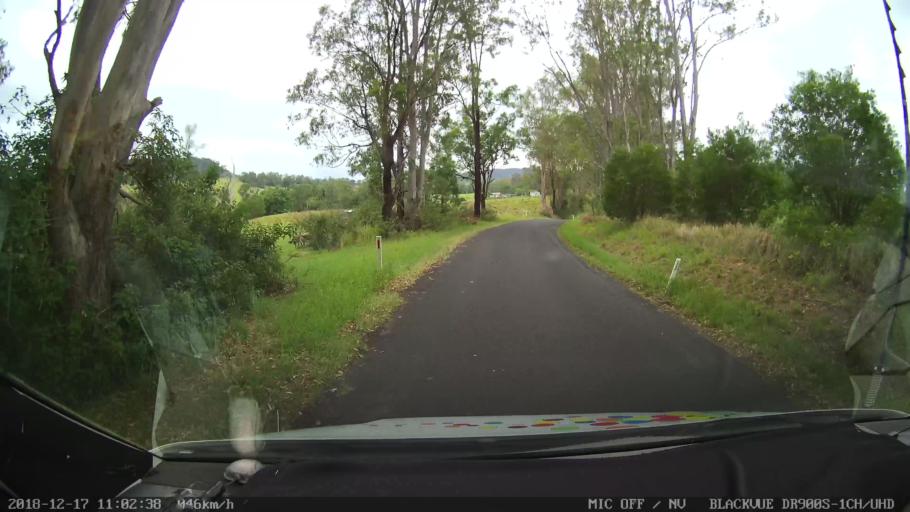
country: AU
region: New South Wales
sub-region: Richmond Valley
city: Casino
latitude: -28.8108
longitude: 152.6330
